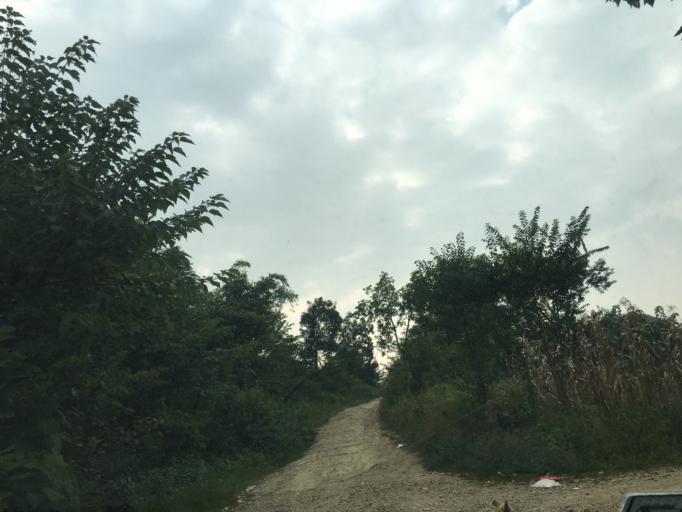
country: CN
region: Guangxi Zhuangzu Zizhiqu
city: Xinzhou
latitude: 25.4451
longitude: 105.6464
